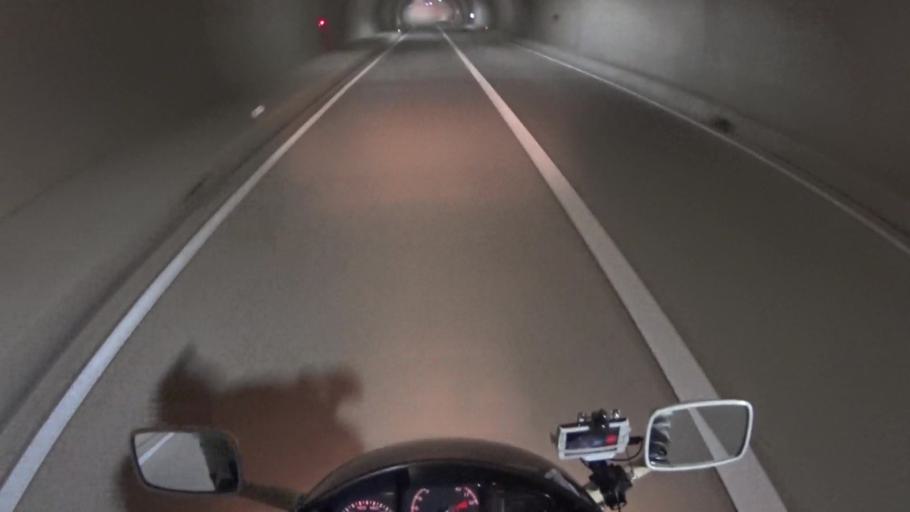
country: JP
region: Kyoto
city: Miyazu
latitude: 35.7408
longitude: 135.2553
